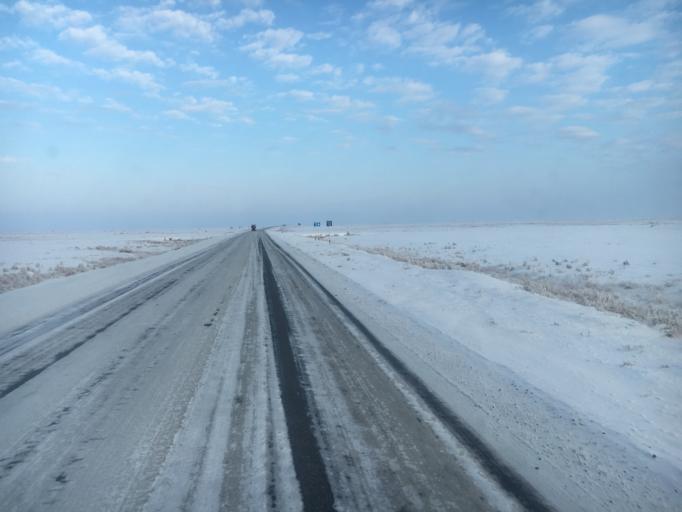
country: KZ
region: Qyzylorda
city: Sekseuil
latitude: 47.8160
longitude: 61.3406
